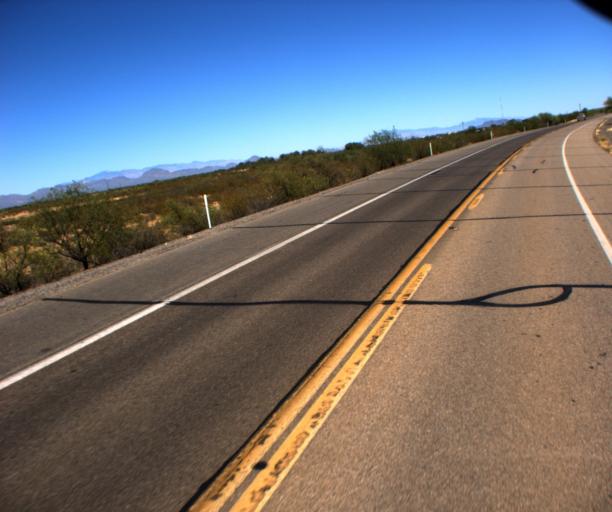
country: US
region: Arizona
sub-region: Pima County
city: Three Points
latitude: 32.0761
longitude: -111.3427
